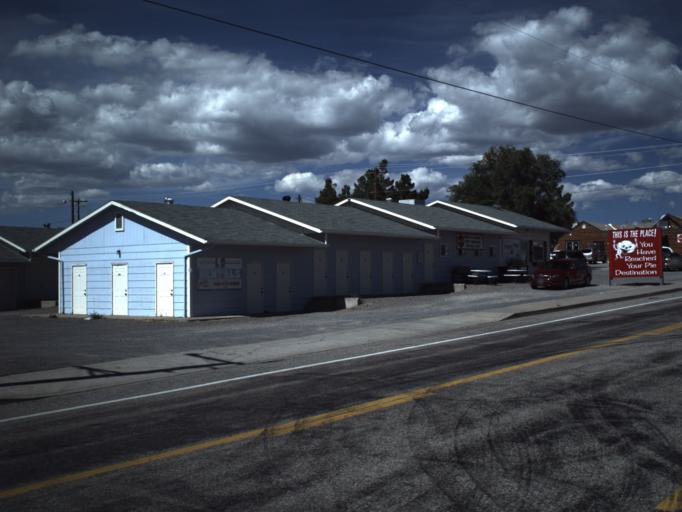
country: US
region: Utah
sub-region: Washington County
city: Ivins
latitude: 37.3371
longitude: -113.6932
